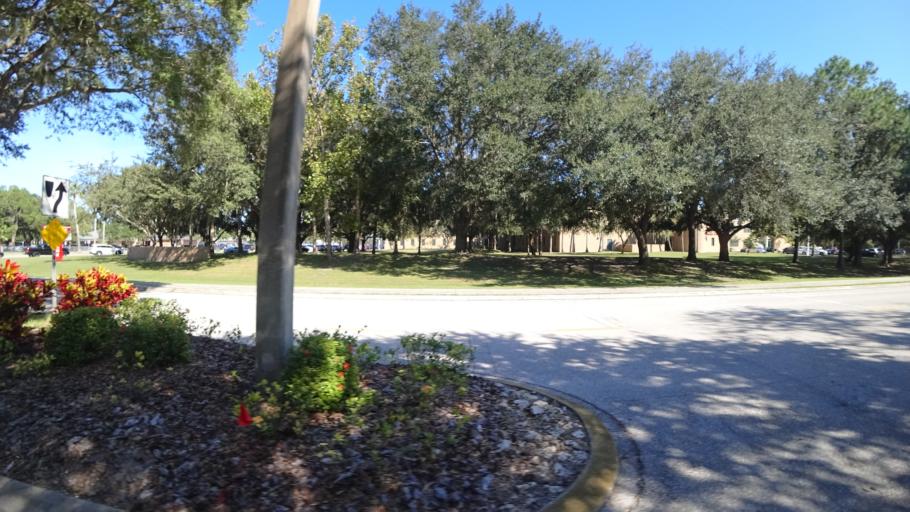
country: US
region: Florida
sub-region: Sarasota County
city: The Meadows
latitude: 27.4303
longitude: -82.4365
